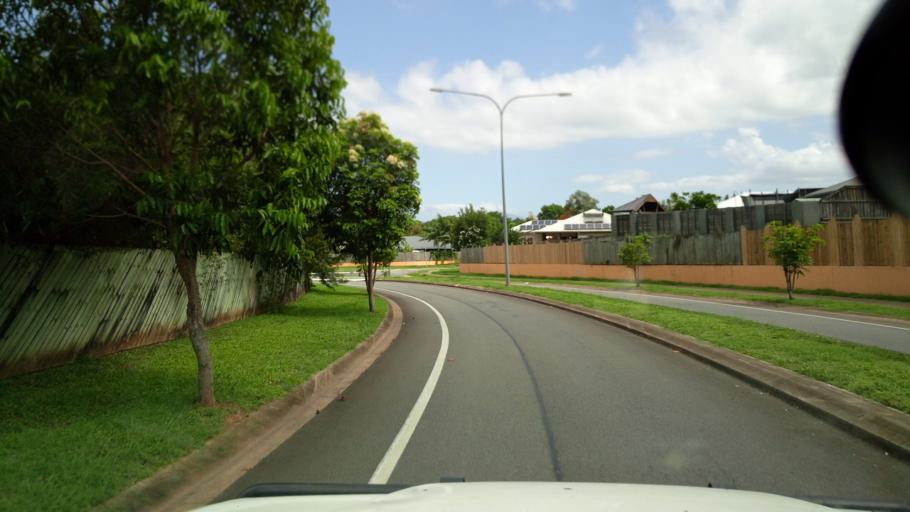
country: AU
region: Queensland
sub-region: Cairns
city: Redlynch
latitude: -16.9182
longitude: 145.7214
